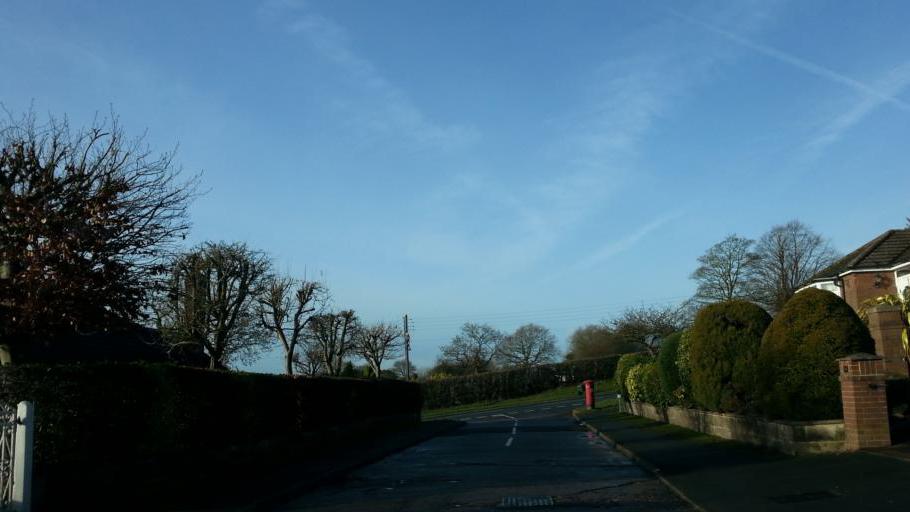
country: GB
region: England
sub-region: Staffordshire
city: Biddulph
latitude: 53.0726
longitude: -2.1411
